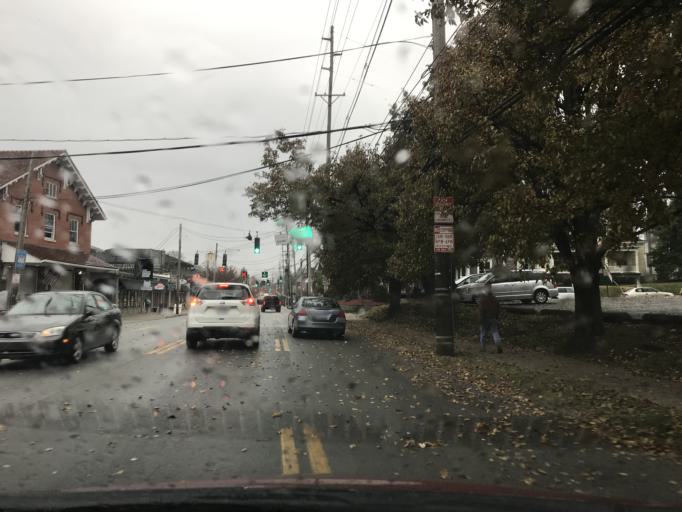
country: US
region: Kentucky
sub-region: Jefferson County
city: Audubon Park
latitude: 38.2292
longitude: -85.7023
